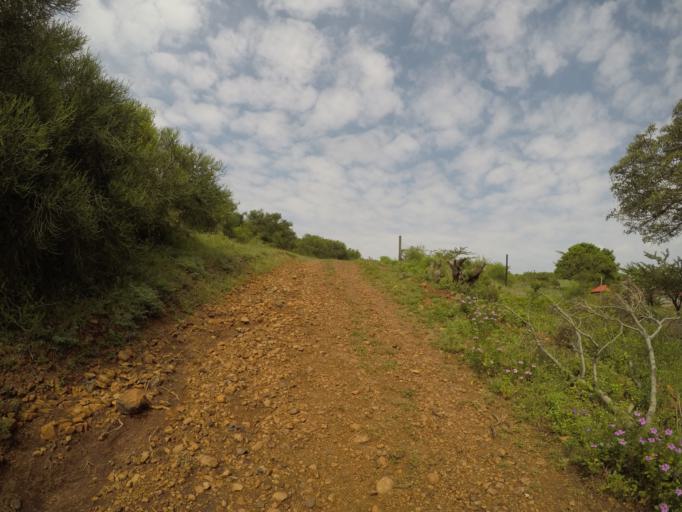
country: ZA
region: KwaZulu-Natal
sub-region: uThungulu District Municipality
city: Empangeni
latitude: -28.6151
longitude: 31.9022
